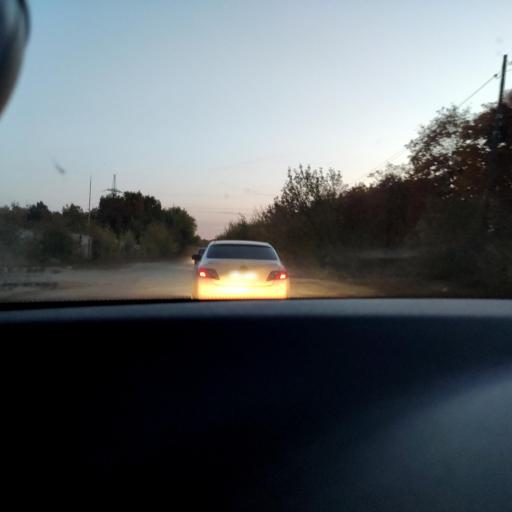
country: RU
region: Samara
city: Novosemeykino
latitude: 53.3442
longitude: 50.3291
